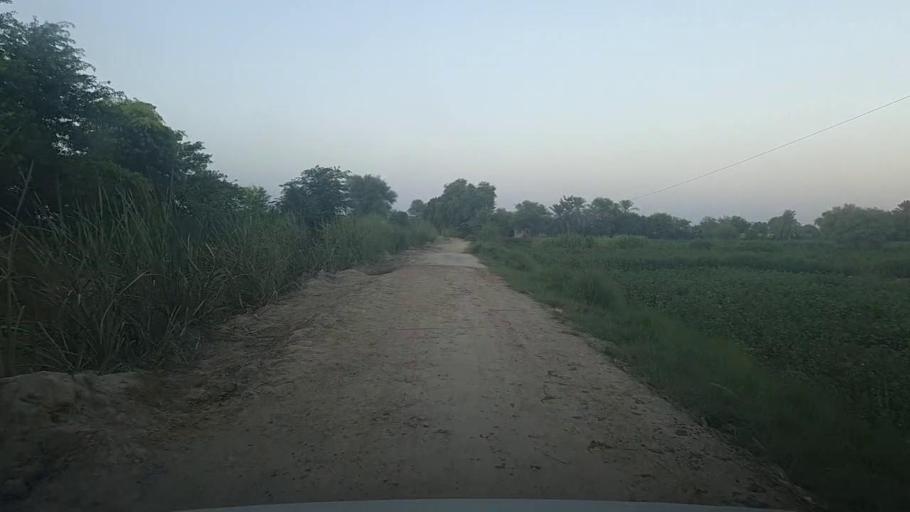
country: PK
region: Sindh
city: Khairpur
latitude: 28.0971
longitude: 69.7391
